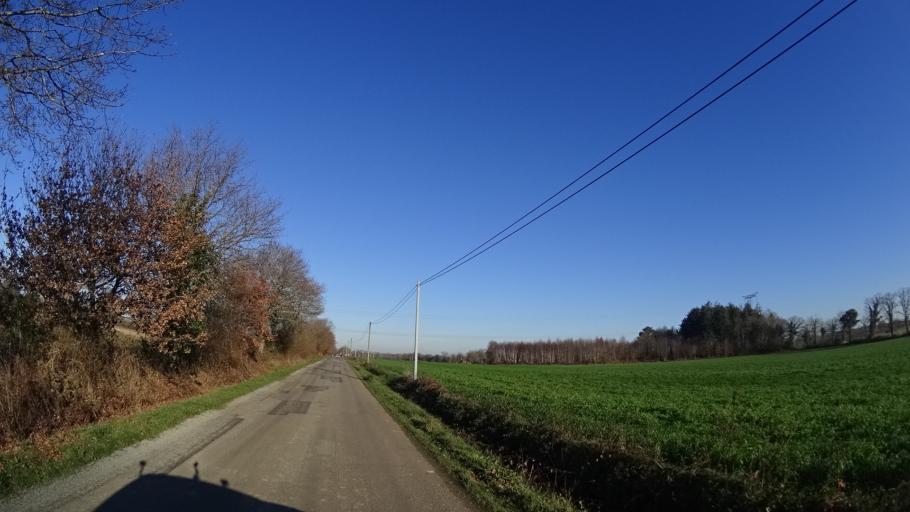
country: FR
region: Brittany
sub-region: Departement du Morbihan
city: Allaire
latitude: 47.6257
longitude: -2.1833
